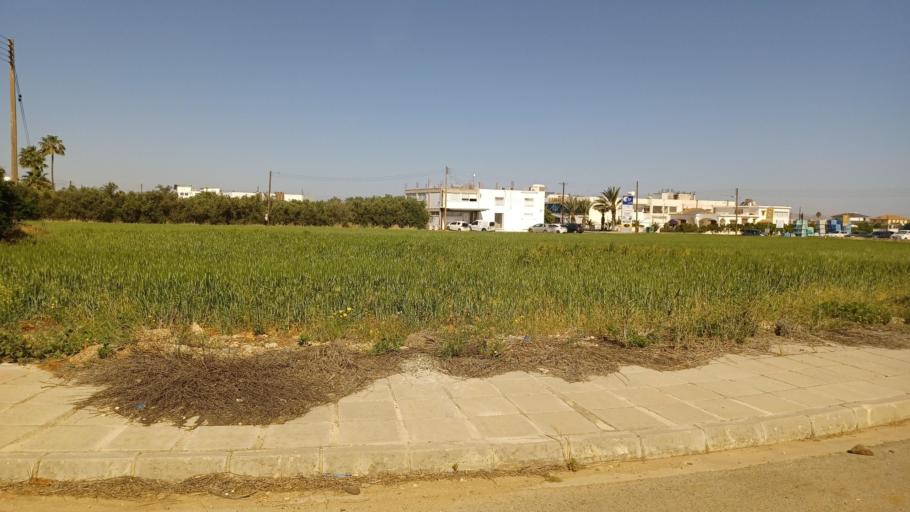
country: CY
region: Lefkosia
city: Kokkinotrimithia
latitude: 35.1480
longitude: 33.2109
